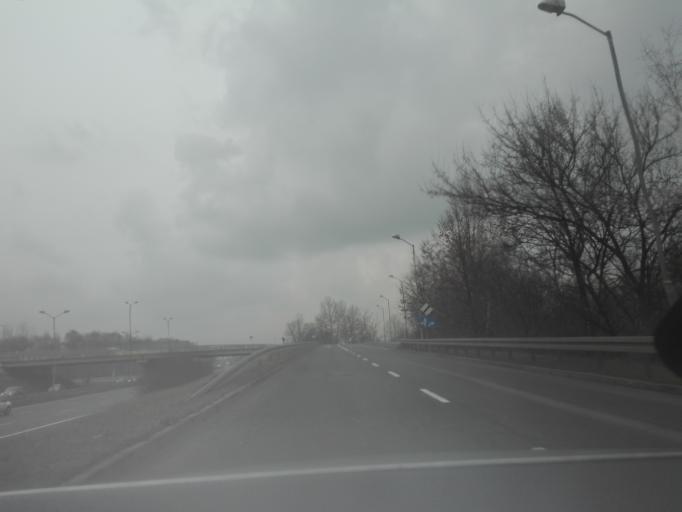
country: PL
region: Silesian Voivodeship
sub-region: Chorzow
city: Chorzow
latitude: 50.2714
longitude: 18.9769
